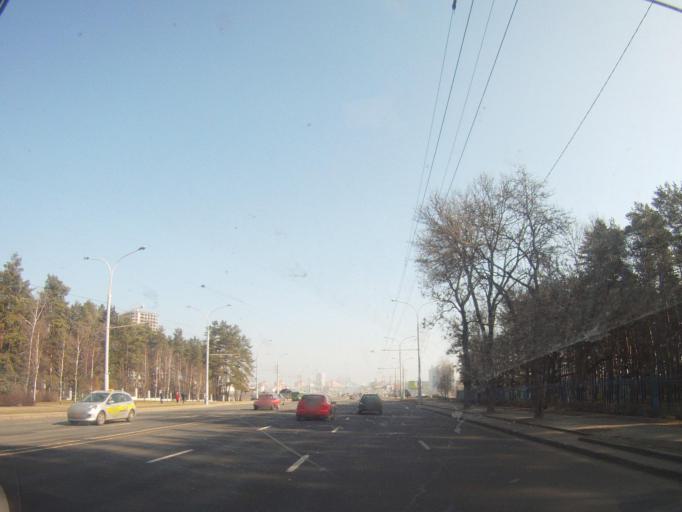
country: BY
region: Minsk
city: Borovlyany
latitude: 53.9376
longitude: 27.6632
